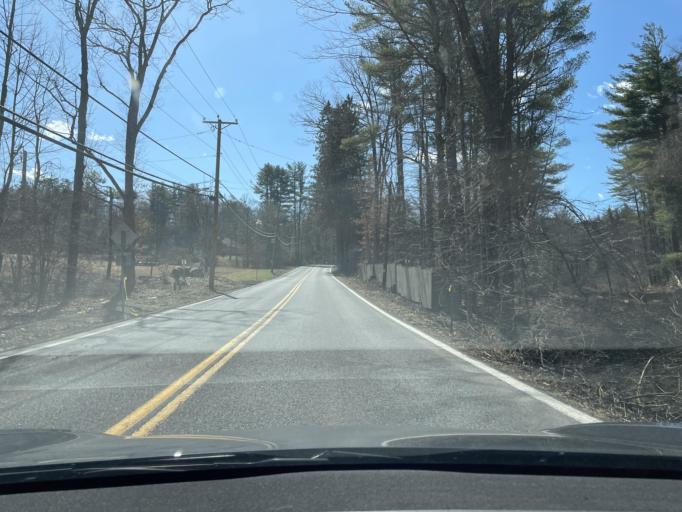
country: US
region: New York
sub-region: Ulster County
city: West Hurley
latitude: 42.0181
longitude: -74.1055
